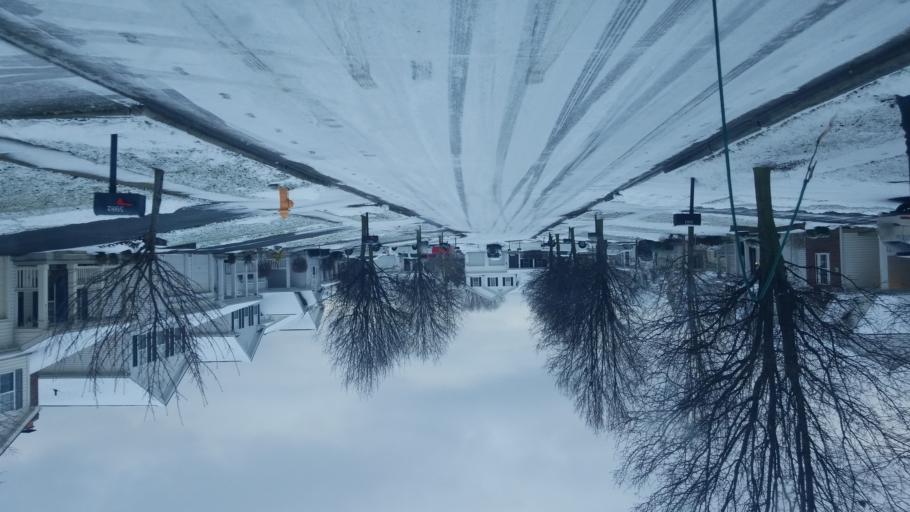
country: US
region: Ohio
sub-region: Franklin County
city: New Albany
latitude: 40.0696
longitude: -82.8584
